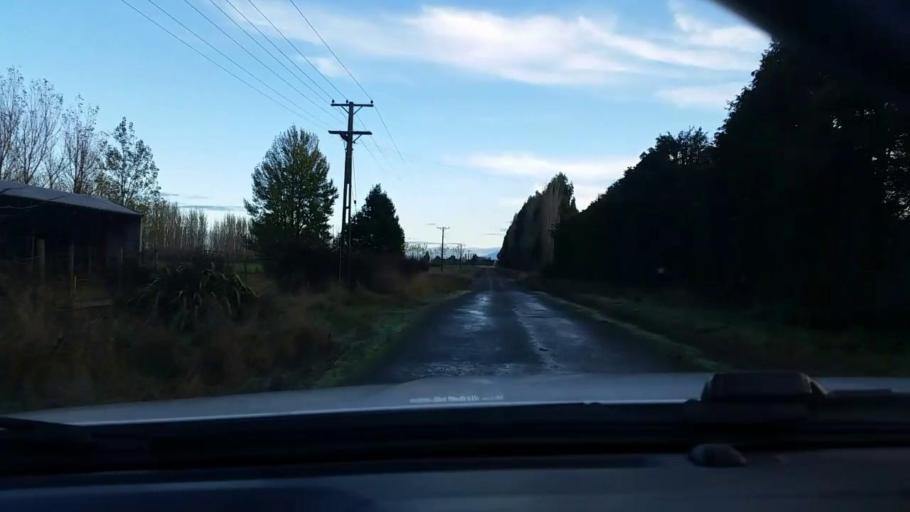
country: NZ
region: Southland
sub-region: Southland District
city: Winton
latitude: -46.1496
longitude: 168.2552
